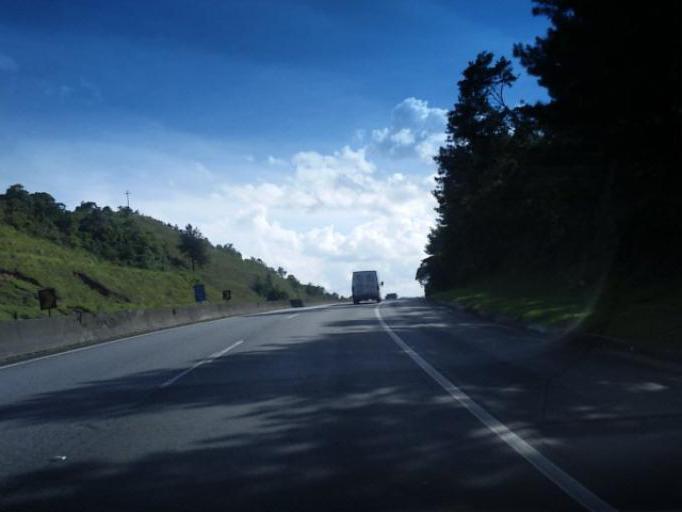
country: BR
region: Parana
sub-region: Campina Grande Do Sul
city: Campina Grande do Sul
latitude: -25.2448
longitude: -48.9029
